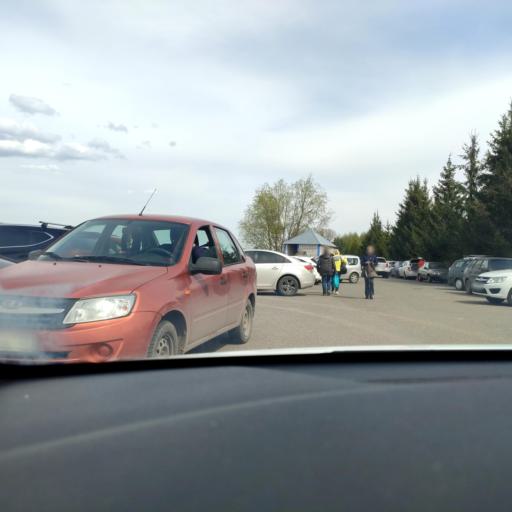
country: RU
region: Tatarstan
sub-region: Gorod Kazan'
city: Kazan
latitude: 55.8895
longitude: 49.0979
